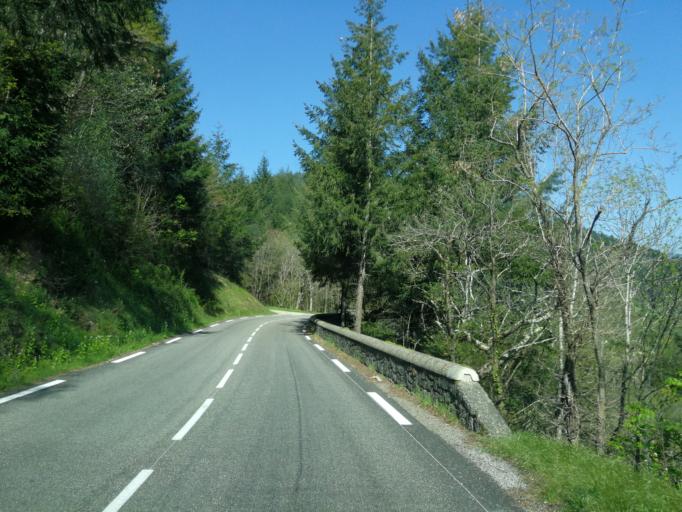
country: FR
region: Rhone-Alpes
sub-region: Departement de l'Ardeche
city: Le Cheylard
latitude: 44.8950
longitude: 4.4890
